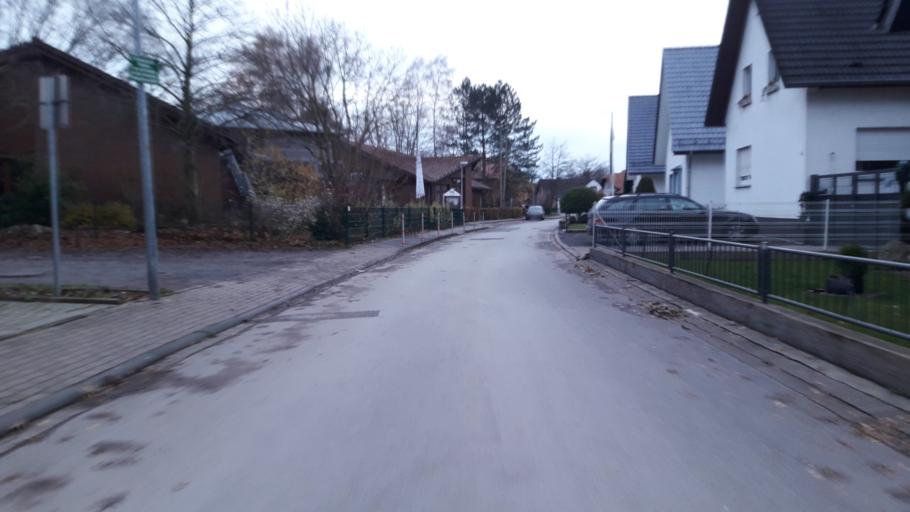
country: DE
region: North Rhine-Westphalia
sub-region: Regierungsbezirk Detmold
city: Hovelhof
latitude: 51.8206
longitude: 8.6503
